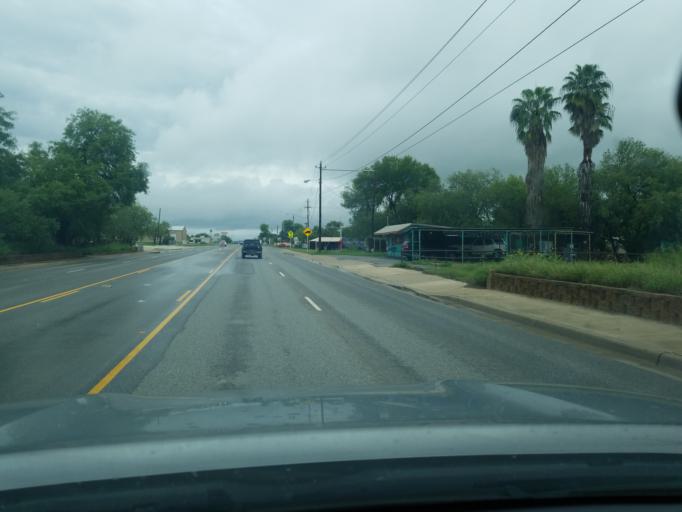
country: US
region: Texas
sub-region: Dimmit County
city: Carrizo Springs
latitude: 28.5300
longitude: -99.8535
